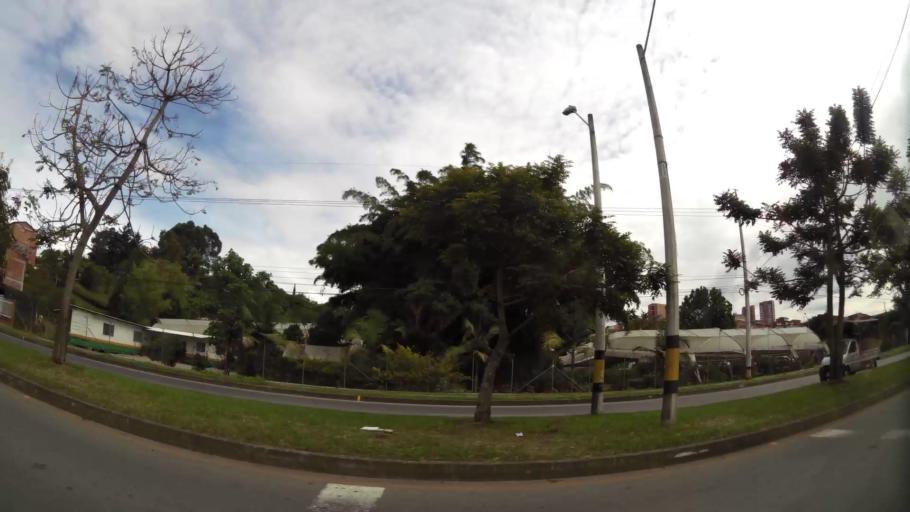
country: CO
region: Antioquia
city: Rionegro
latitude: 6.1515
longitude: -75.3684
